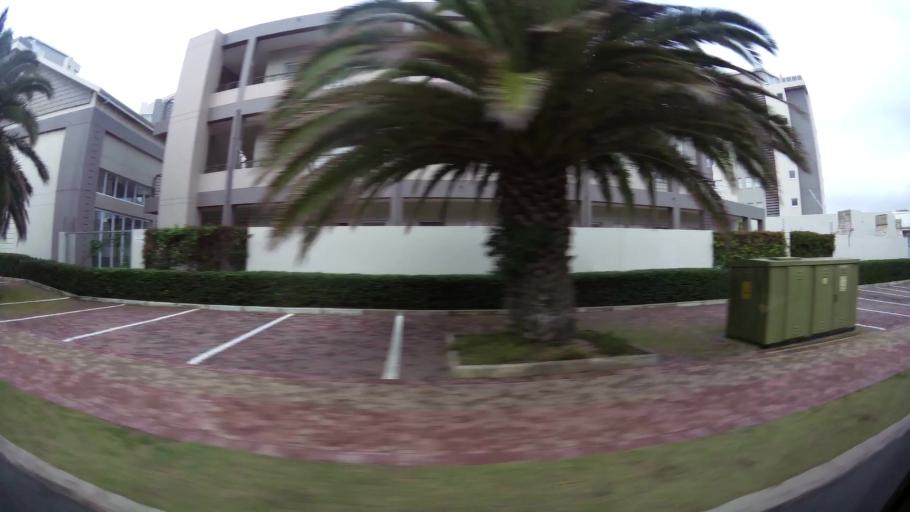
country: ZA
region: Western Cape
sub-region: Eden District Municipality
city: Mossel Bay
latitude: -34.1622
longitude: 22.1091
